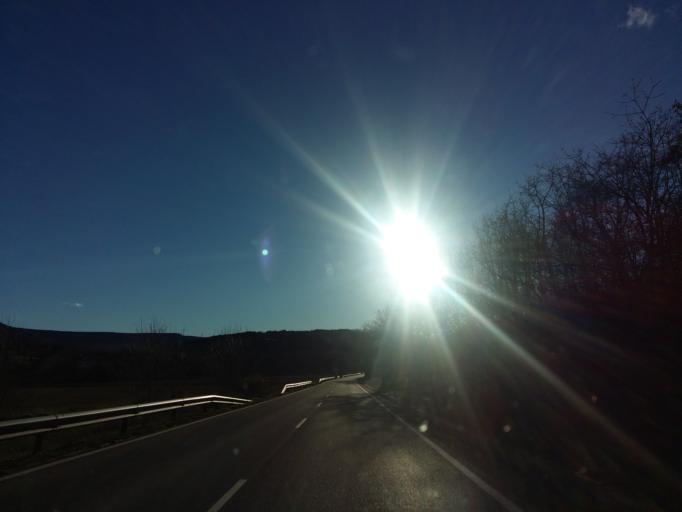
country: ES
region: Cantabria
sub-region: Provincia de Cantabria
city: San Martin de Elines
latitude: 42.8224
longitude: -3.9095
